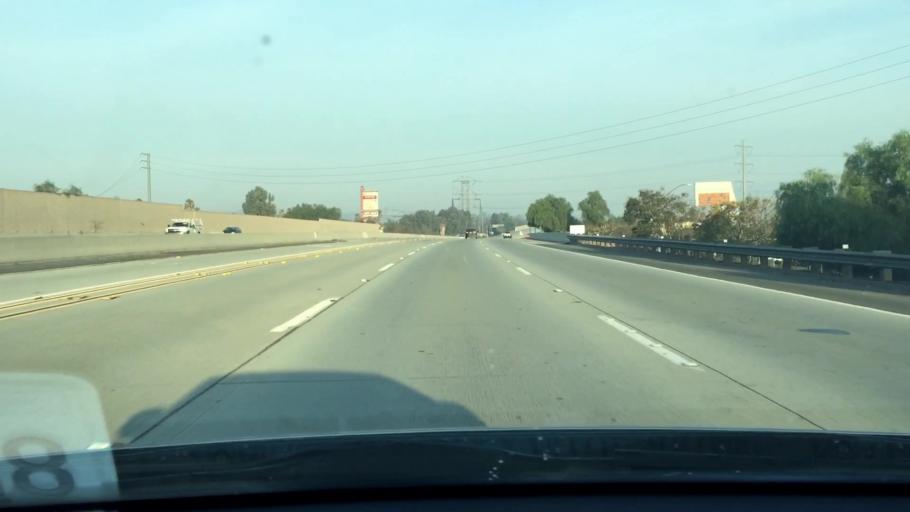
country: US
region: California
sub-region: San Bernardino County
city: Los Serranos
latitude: 33.9822
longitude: -117.7074
